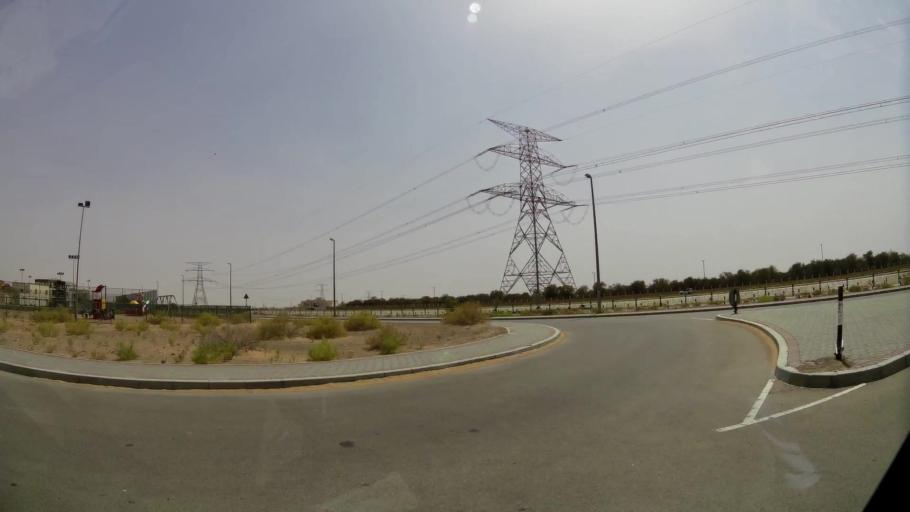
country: AE
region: Abu Dhabi
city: Al Ain
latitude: 24.1661
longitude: 55.6559
